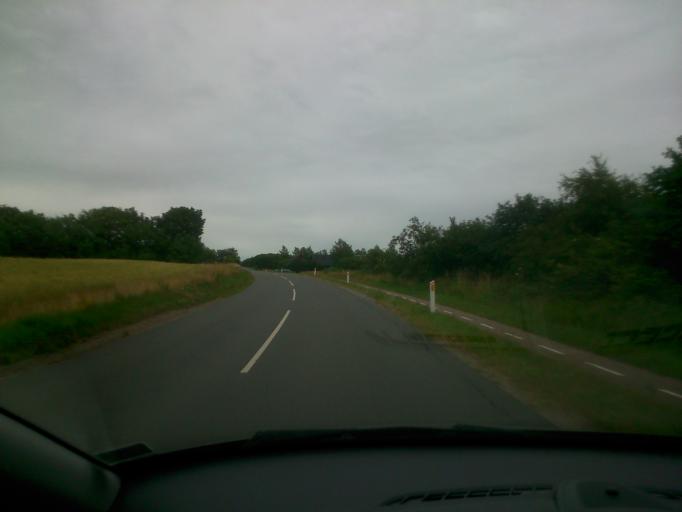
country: DK
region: Central Jutland
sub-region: Ringkobing-Skjern Kommune
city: Skjern
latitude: 55.9489
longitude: 8.4137
